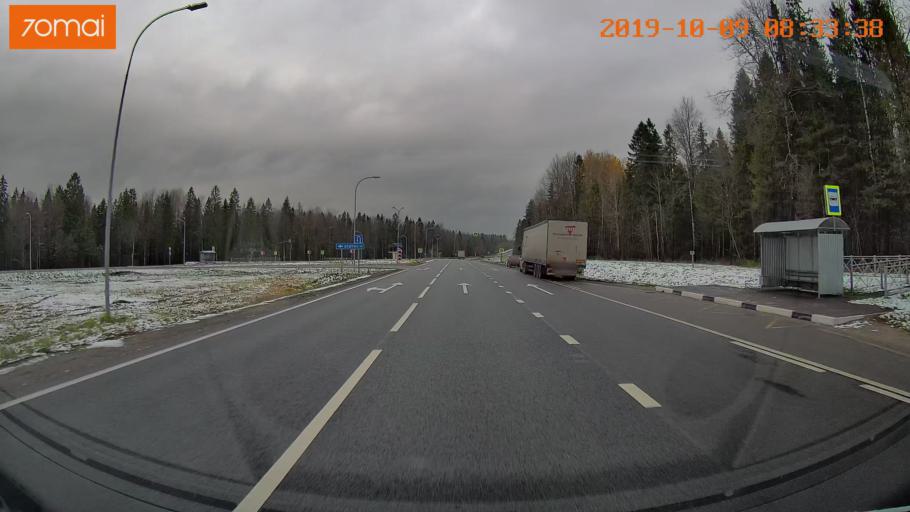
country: RU
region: Vologda
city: Gryazovets
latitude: 58.8852
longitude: 40.1915
